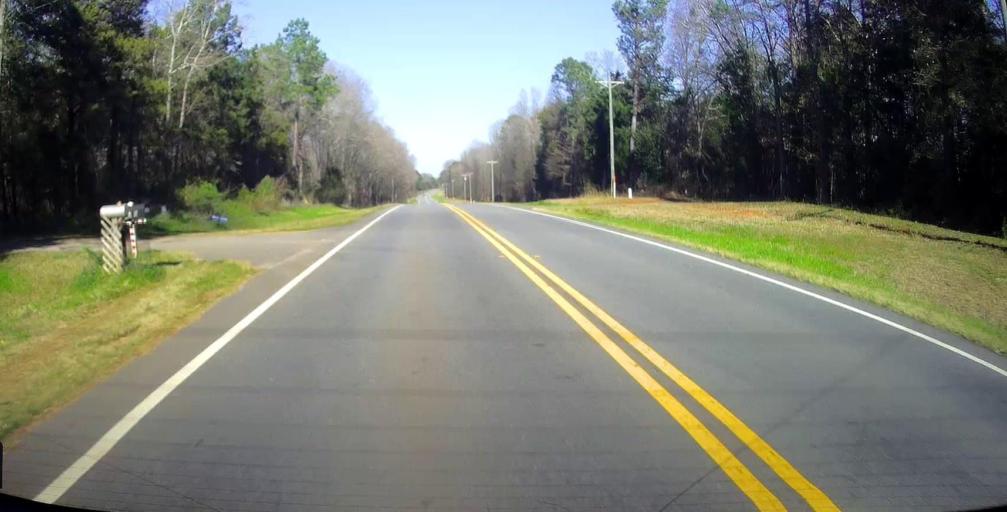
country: US
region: Georgia
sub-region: Macon County
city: Montezuma
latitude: 32.3136
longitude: -83.8987
